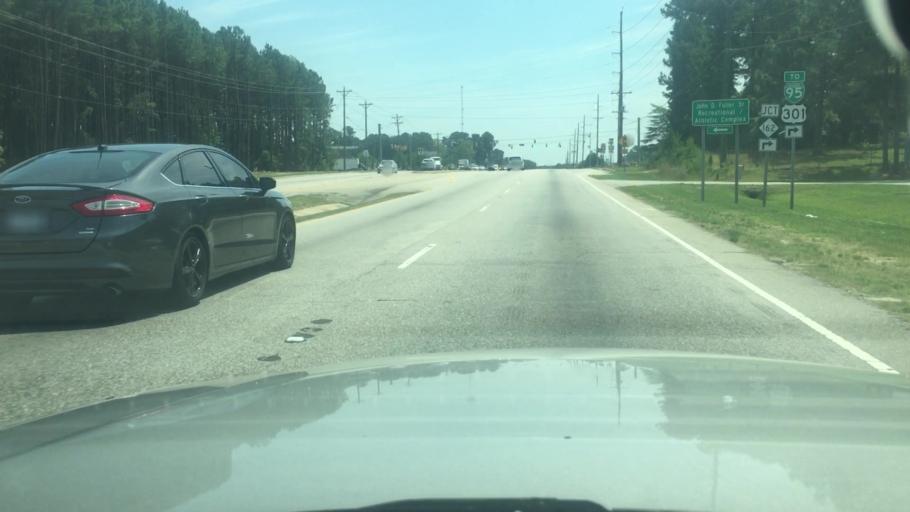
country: US
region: North Carolina
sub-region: Cumberland County
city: Hope Mills
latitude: 35.0416
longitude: -78.9926
